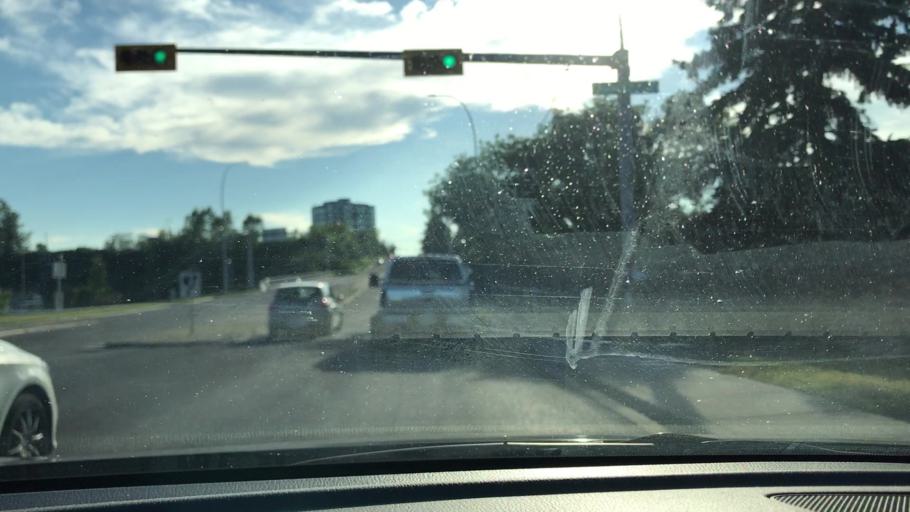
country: CA
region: Alberta
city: Calgary
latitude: 51.0379
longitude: -114.1113
